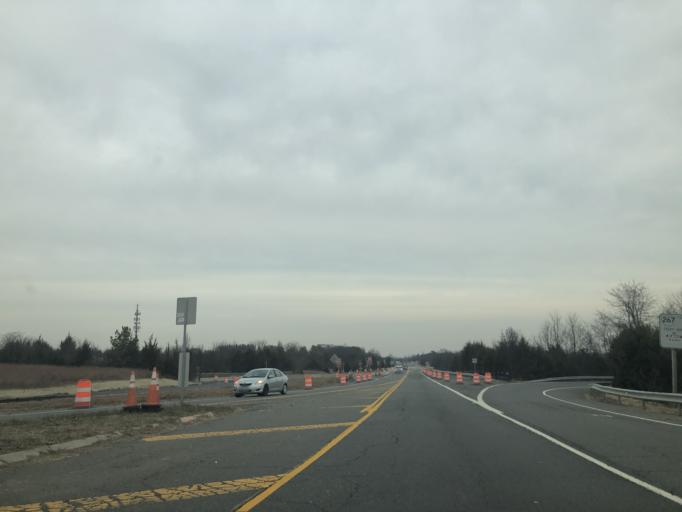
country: US
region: Virginia
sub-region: Loudoun County
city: Broadlands
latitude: 39.0342
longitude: -77.5245
